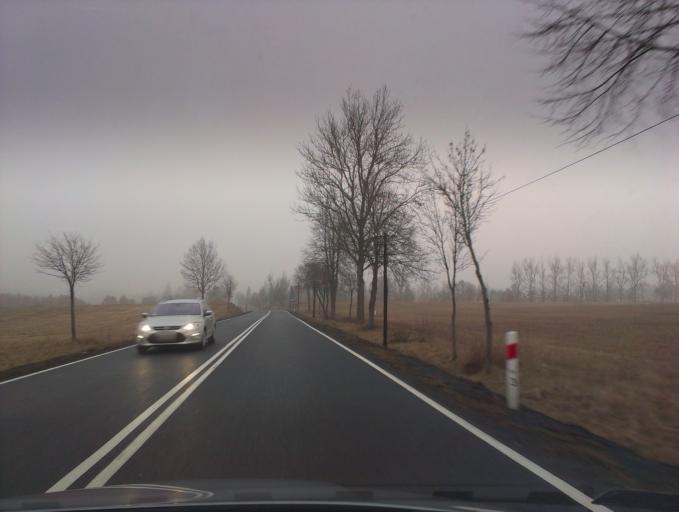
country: PL
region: West Pomeranian Voivodeship
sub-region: Powiat szczecinecki
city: Szczecinek
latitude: 53.8064
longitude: 16.6420
